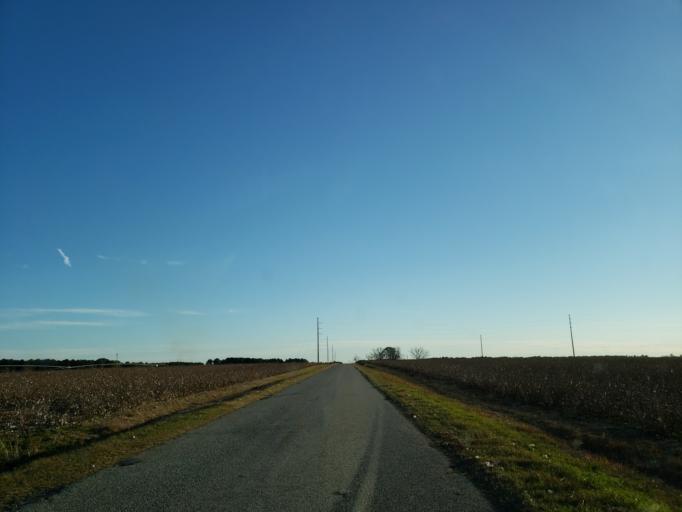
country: US
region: Georgia
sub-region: Dooly County
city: Vienna
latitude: 32.1472
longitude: -83.7610
